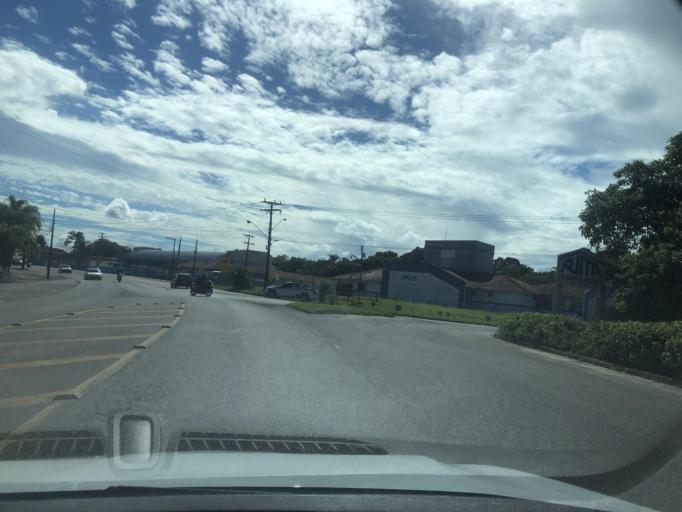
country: BR
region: Santa Catarina
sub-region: Sao Francisco Do Sul
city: Sao Francisco do Sul
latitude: -26.2053
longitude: -48.5383
